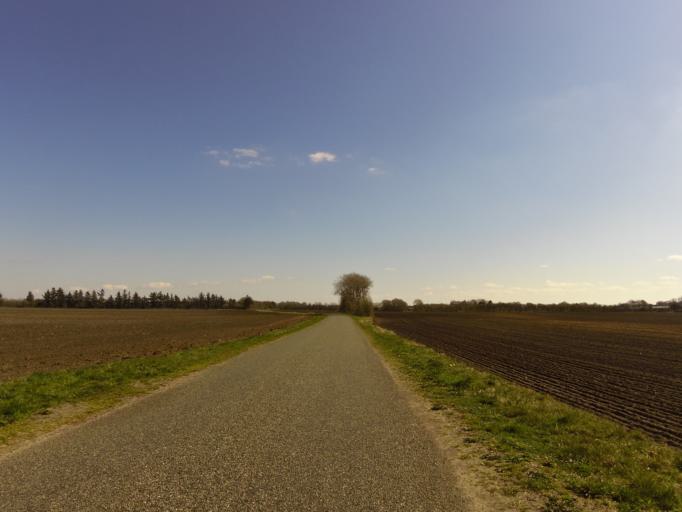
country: DK
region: South Denmark
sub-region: Esbjerg Kommune
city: Ribe
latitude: 55.3385
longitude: 8.8695
